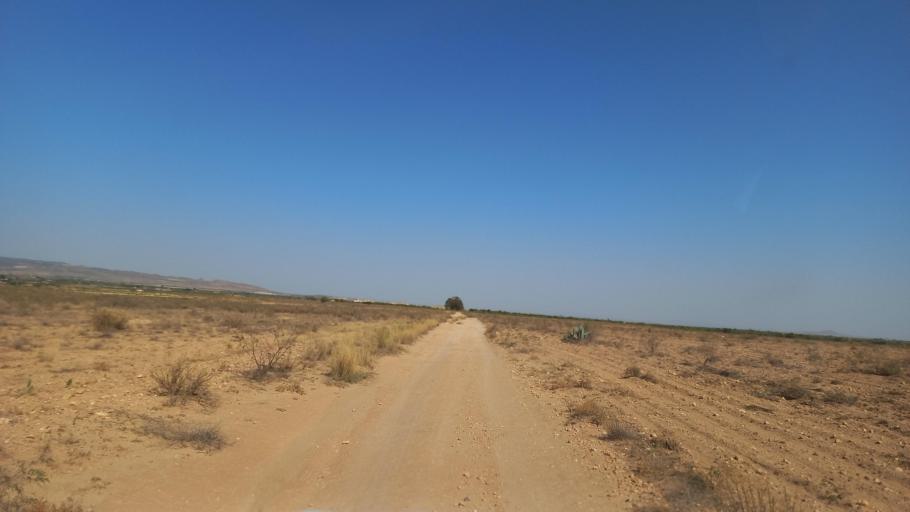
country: TN
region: Al Qasrayn
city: Kasserine
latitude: 35.2168
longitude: 9.0281
